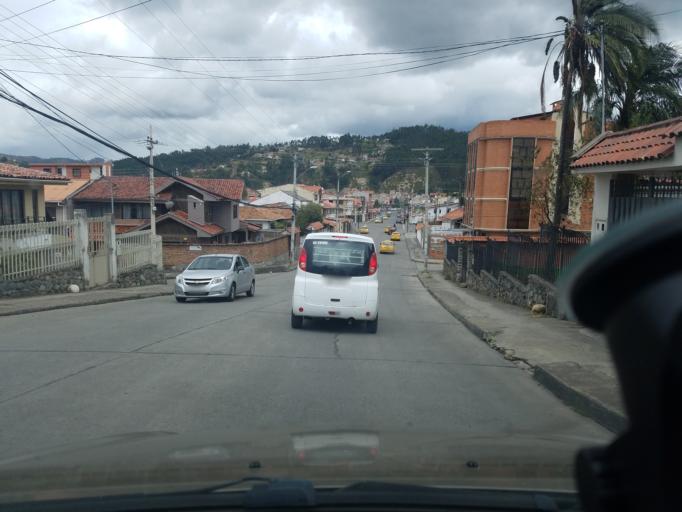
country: EC
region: Azuay
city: Cuenca
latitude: -2.9021
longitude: -78.9890
